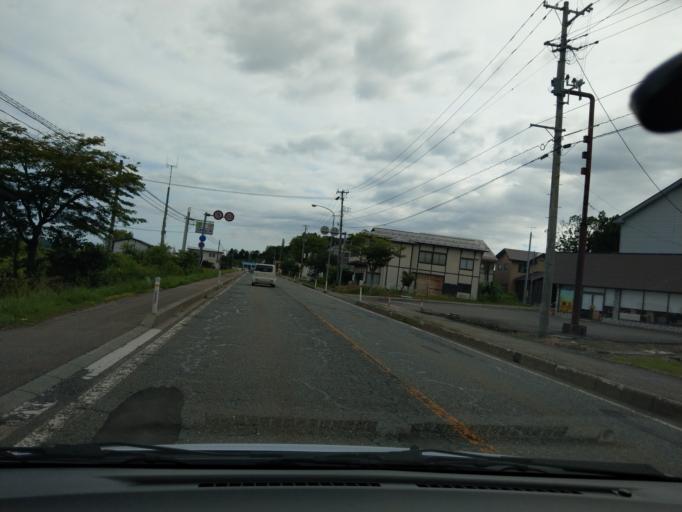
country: JP
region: Akita
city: Yokotemachi
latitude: 39.3506
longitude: 140.5622
